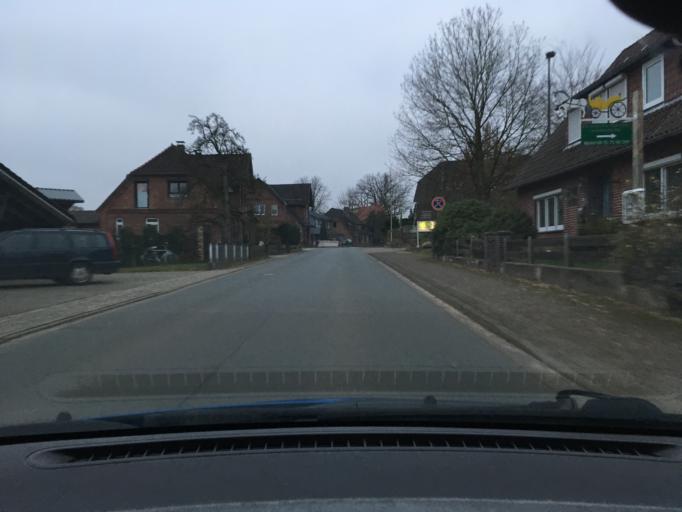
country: DE
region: Lower Saxony
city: Bispingen
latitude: 53.1117
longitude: 9.9618
